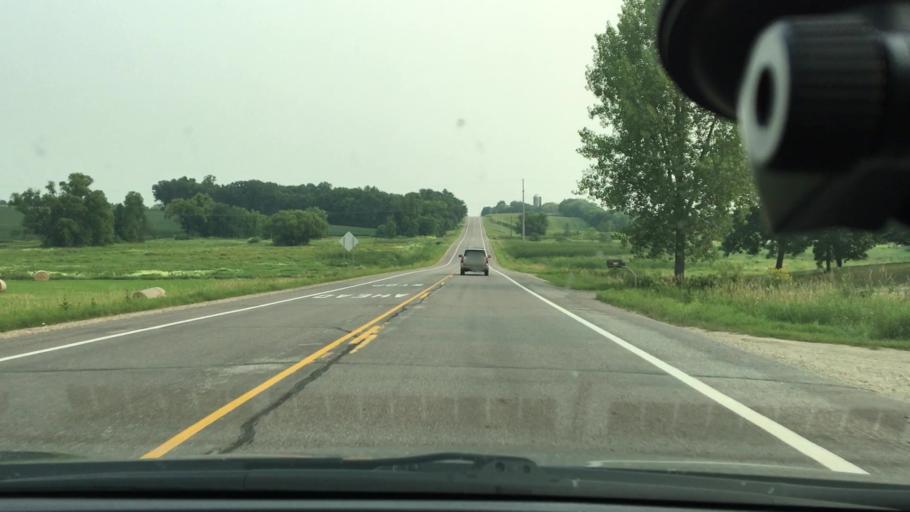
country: US
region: Minnesota
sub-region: Wright County
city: Albertville
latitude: 45.2872
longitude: -93.6637
